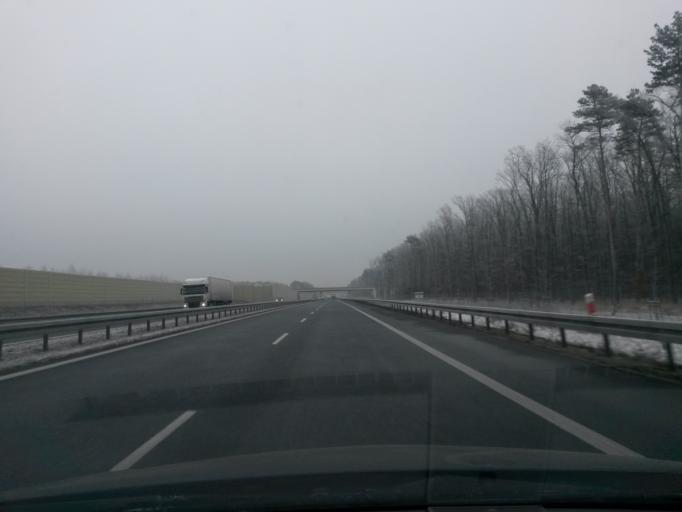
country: PL
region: Greater Poland Voivodeship
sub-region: Powiat poznanski
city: Pobiedziska
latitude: 52.4419
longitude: 17.3492
